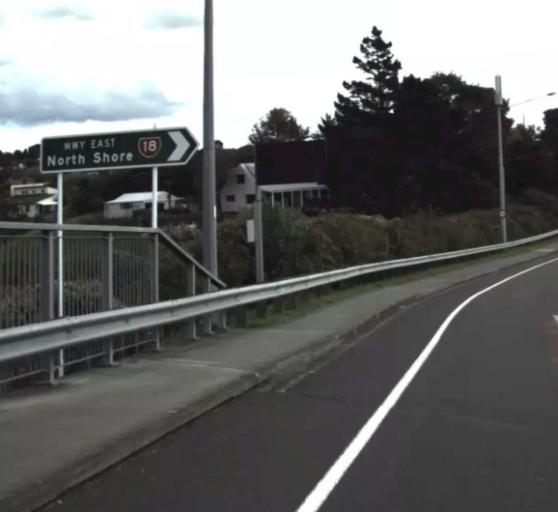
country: NZ
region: Auckland
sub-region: Auckland
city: North Shore
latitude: -36.7715
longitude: 174.6857
